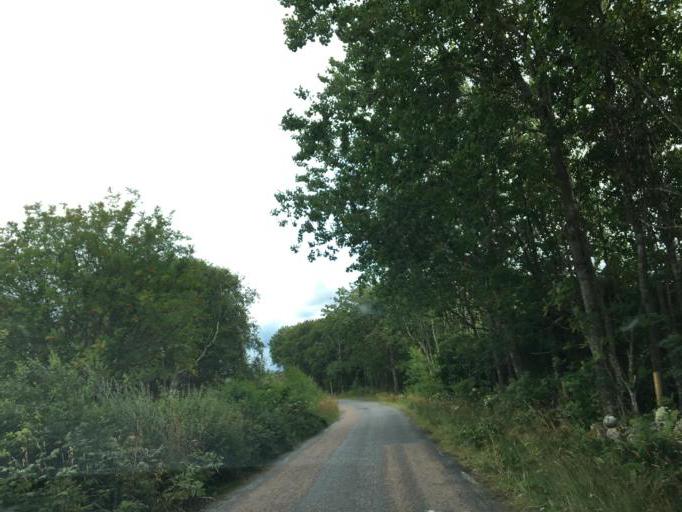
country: SE
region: Vaestra Goetaland
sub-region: Sotenas Kommun
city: Kungshamn
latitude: 58.4102
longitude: 11.2568
